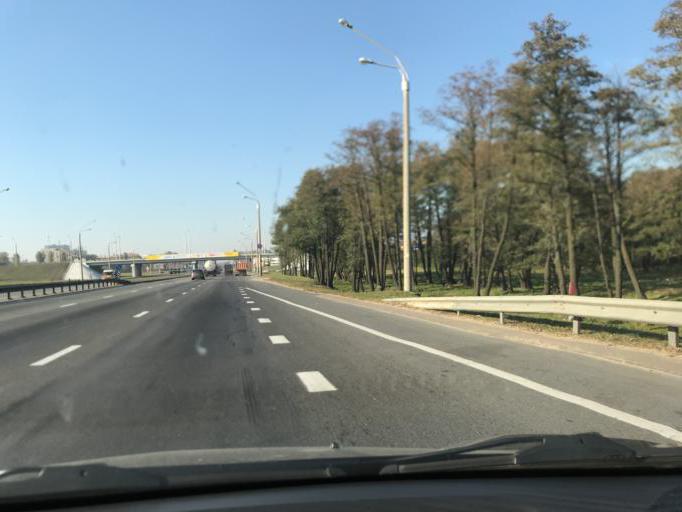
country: BY
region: Minsk
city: Vyaliki Trastsyanets
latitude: 53.8447
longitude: 27.7130
